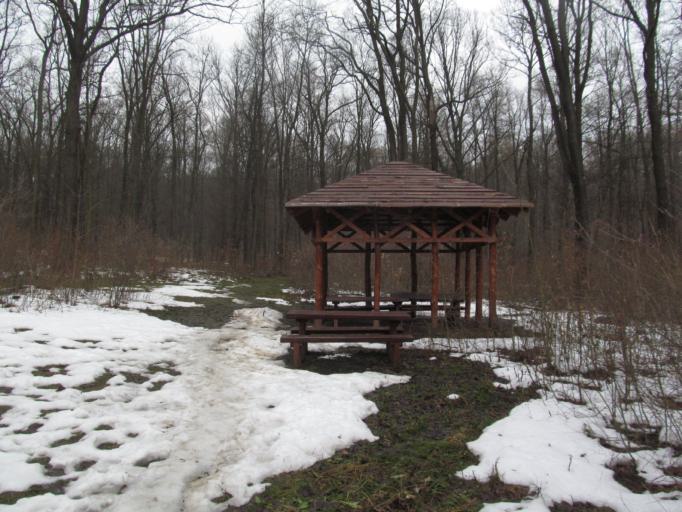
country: HU
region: Veszprem
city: Zirc
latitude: 47.2668
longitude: 17.8613
